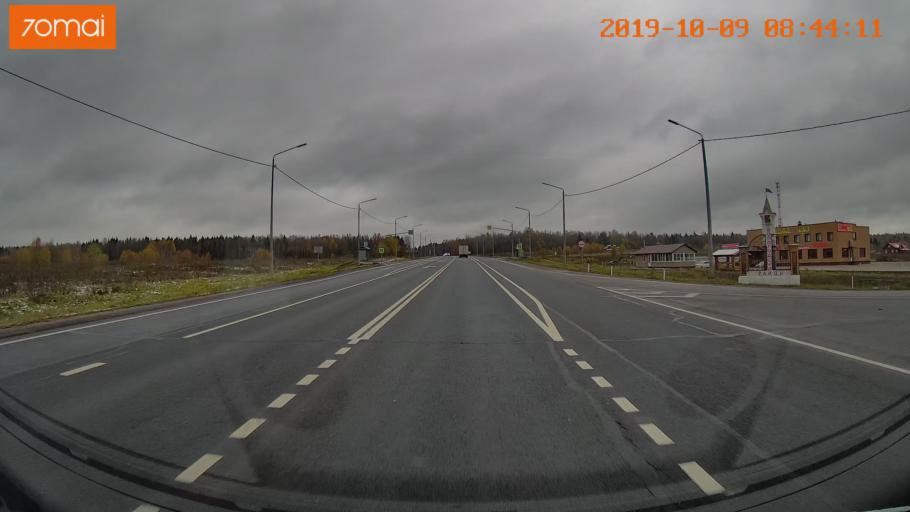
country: RU
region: Vologda
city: Gryazovets
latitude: 59.0331
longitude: 40.1099
